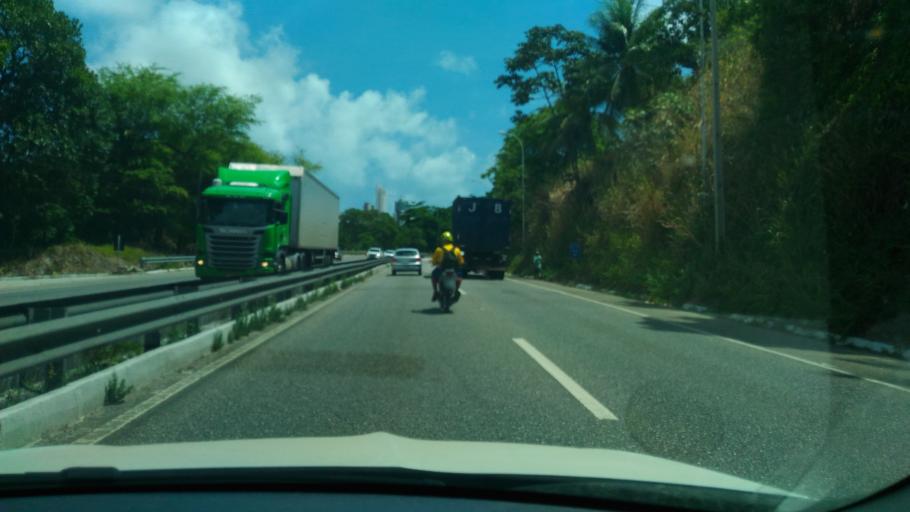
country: BR
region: Paraiba
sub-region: Joao Pessoa
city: Joao Pessoa
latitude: -7.1298
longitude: -34.8507
